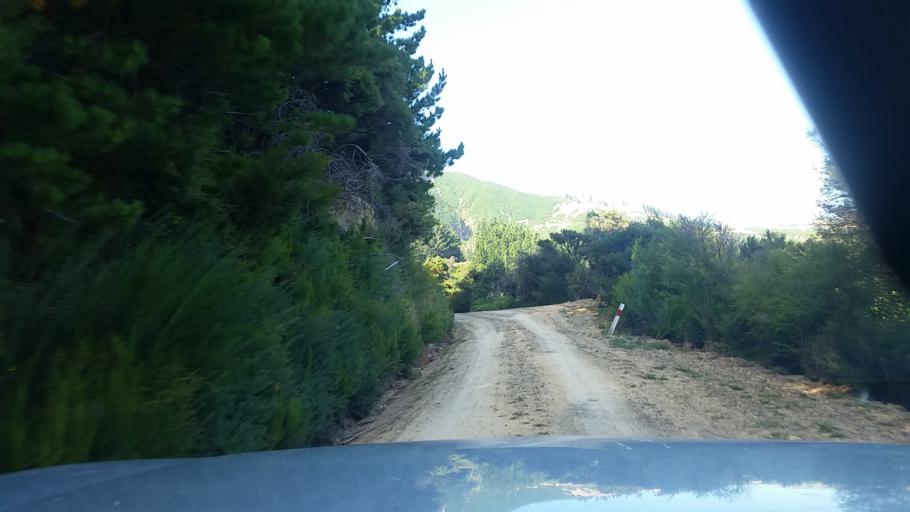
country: NZ
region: Marlborough
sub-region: Marlborough District
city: Picton
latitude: -41.3113
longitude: 174.1716
